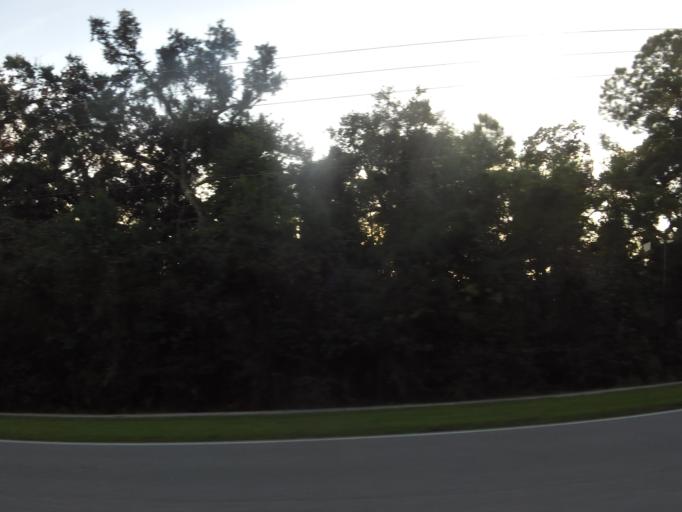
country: US
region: Florida
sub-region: Saint Johns County
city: Palm Valley
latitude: 30.1596
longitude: -81.3843
